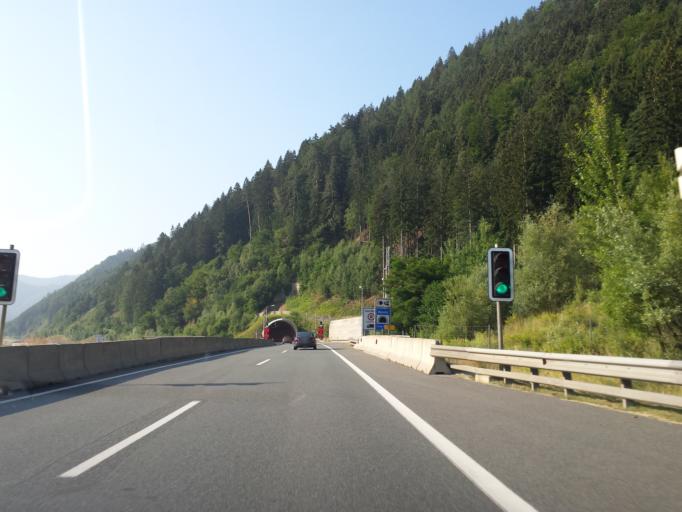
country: AT
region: Styria
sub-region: Politischer Bezirk Graz-Umgebung
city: Rothelstein
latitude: 47.3355
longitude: 15.3515
